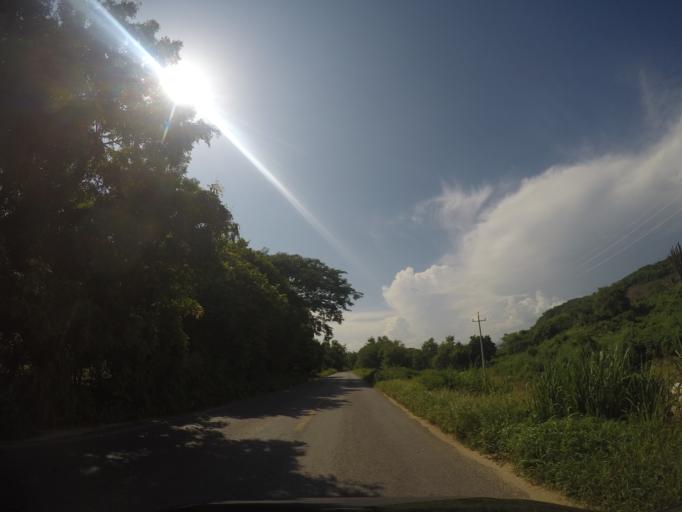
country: MX
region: Oaxaca
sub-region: San Pedro Mixtepec -Dto. 22 -
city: Puerto Escondido
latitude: 15.8901
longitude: -97.1163
